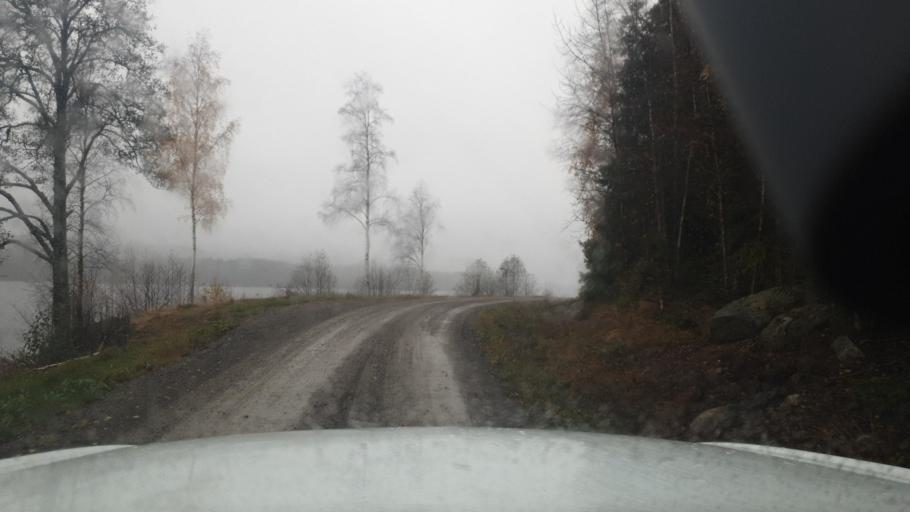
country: SE
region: Vaermland
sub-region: Arvika Kommun
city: Arvika
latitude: 59.8656
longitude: 12.8189
